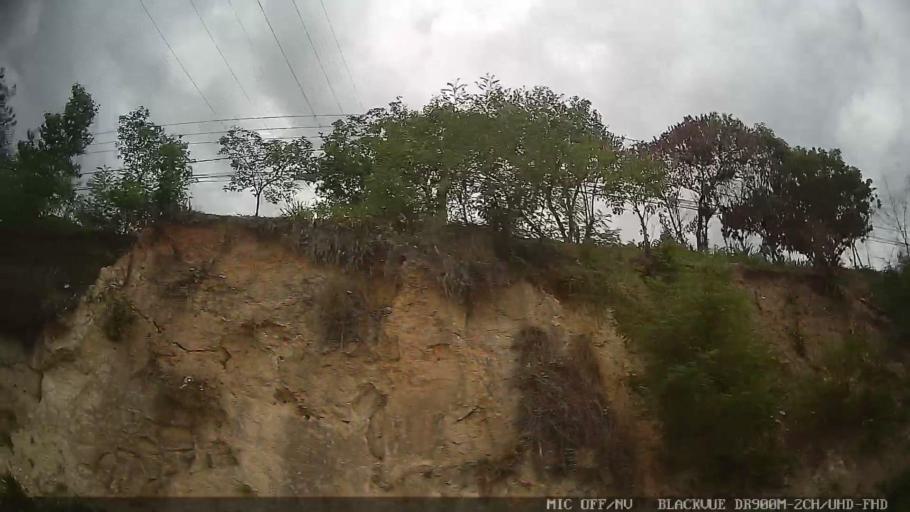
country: BR
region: Sao Paulo
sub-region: Amparo
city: Amparo
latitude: -22.7180
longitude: -46.7839
